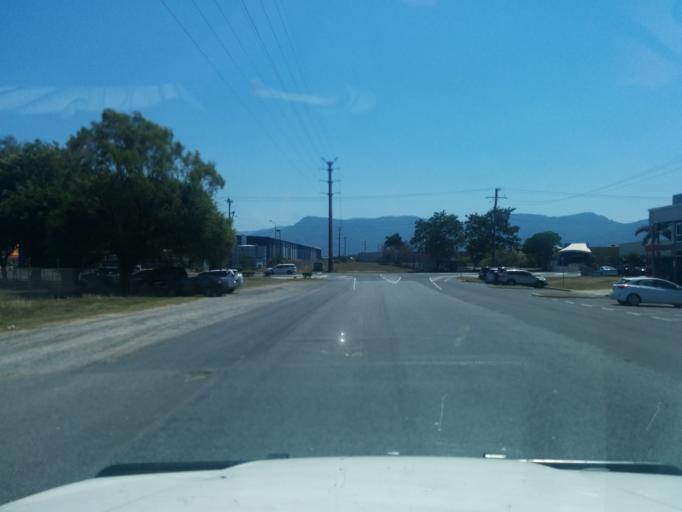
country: AU
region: Queensland
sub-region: Cairns
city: Cairns
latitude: -16.9304
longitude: 145.7731
